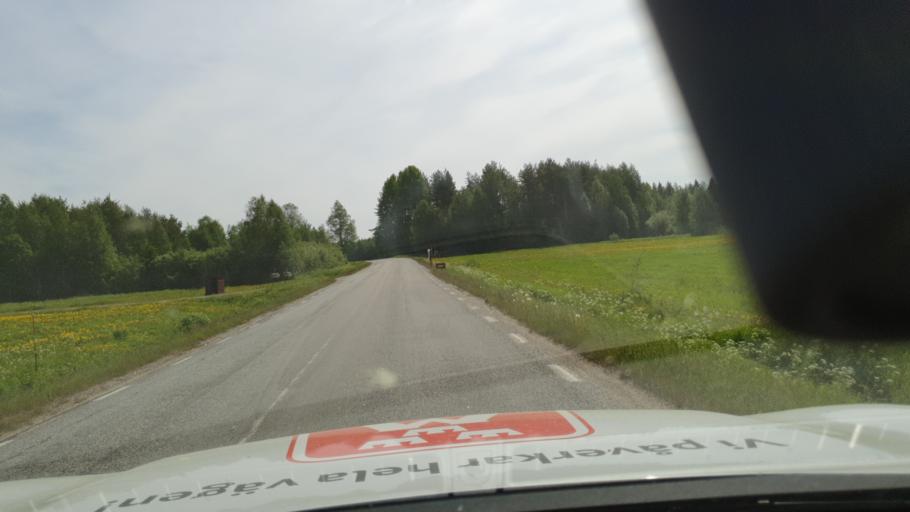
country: SE
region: Vaesterbotten
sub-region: Robertsfors Kommun
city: Robertsfors
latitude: 64.2847
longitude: 20.9350
